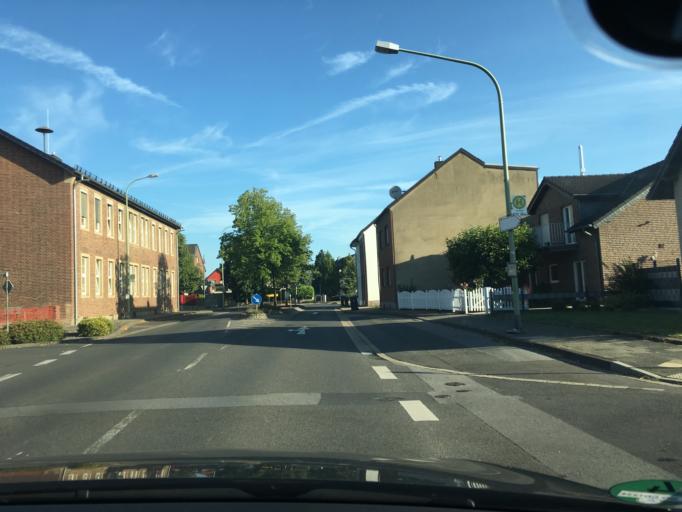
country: DE
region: North Rhine-Westphalia
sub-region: Regierungsbezirk Koln
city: Niederzier
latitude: 50.8666
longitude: 6.4753
